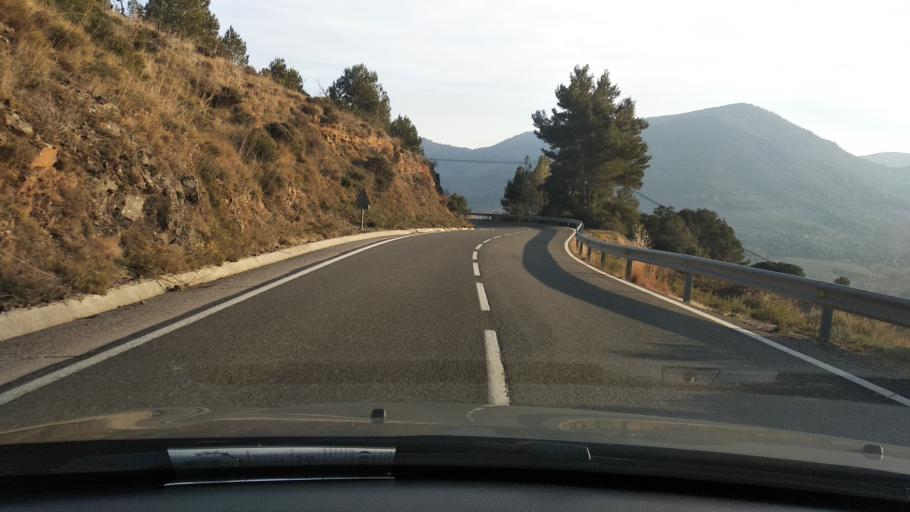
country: ES
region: Catalonia
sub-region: Provincia de Tarragona
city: Alforja
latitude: 41.2195
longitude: 0.9506
